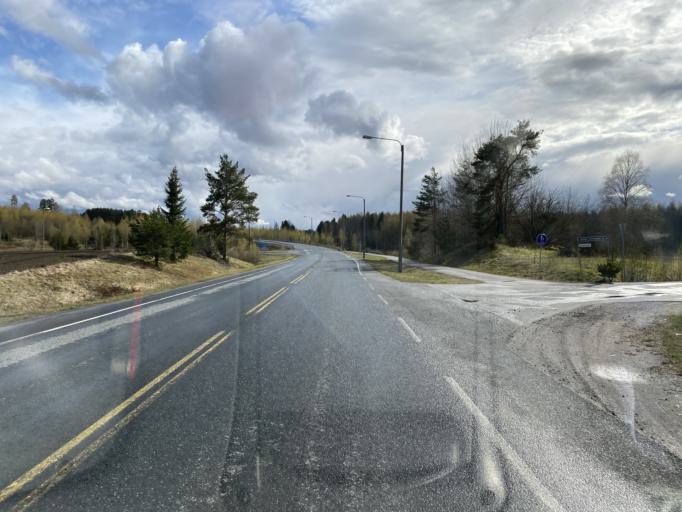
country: FI
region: Pirkanmaa
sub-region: Etelae-Pirkanmaa
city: Kylmaekoski
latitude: 61.1883
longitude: 23.7172
